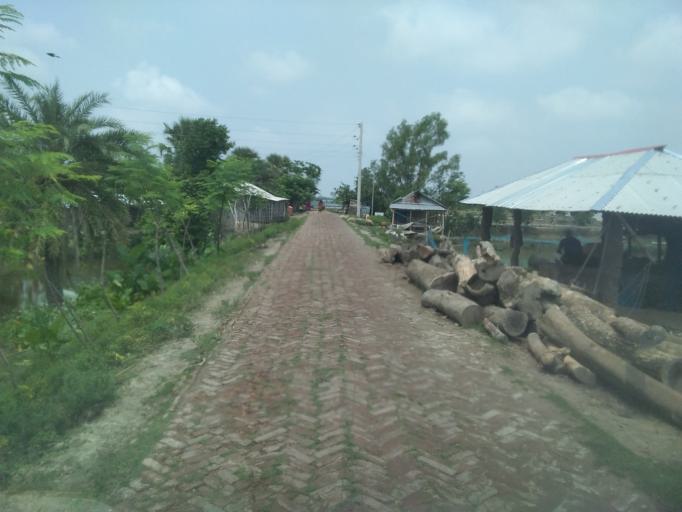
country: BD
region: Khulna
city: Phultala
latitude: 22.6422
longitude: 89.4201
